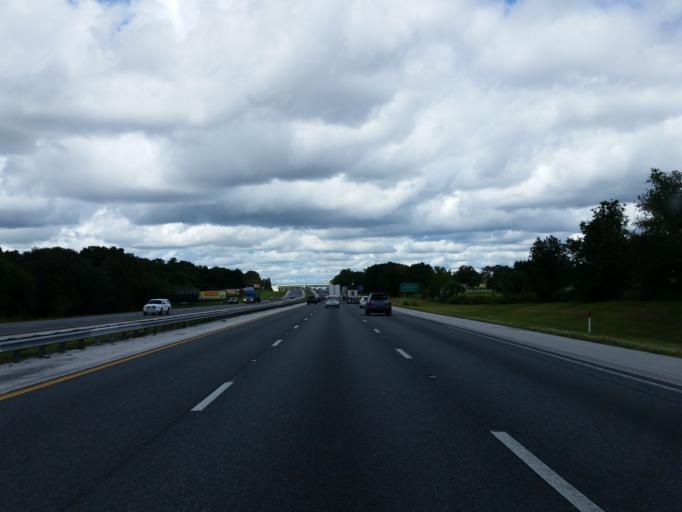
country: US
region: Florida
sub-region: Marion County
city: Ocala
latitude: 29.1333
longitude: -82.1846
